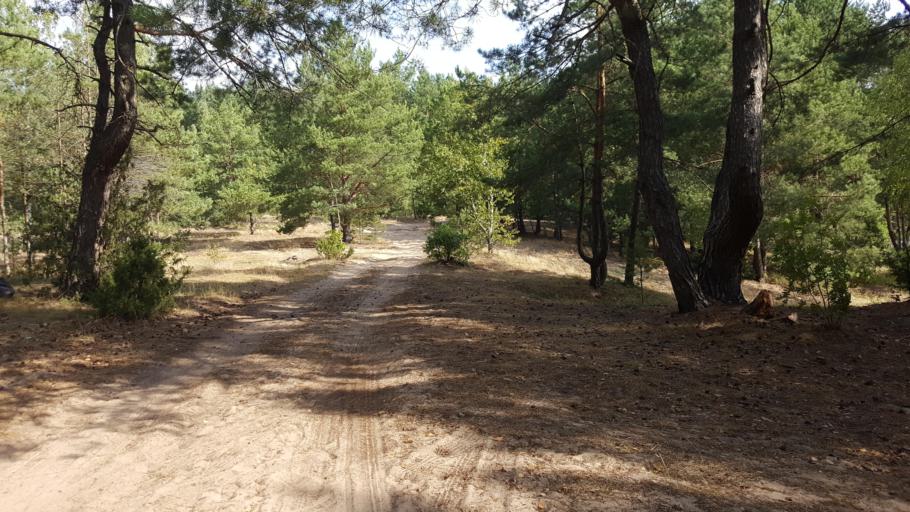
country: BY
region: Brest
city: Ivatsevichy
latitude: 52.7930
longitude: 25.5546
